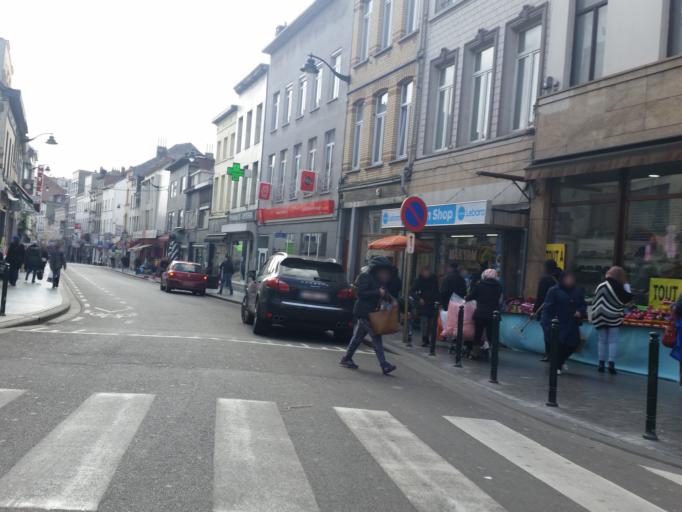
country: BE
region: Brussels Capital
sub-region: Bruxelles-Capitale
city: Brussels
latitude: 50.8555
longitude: 4.3354
